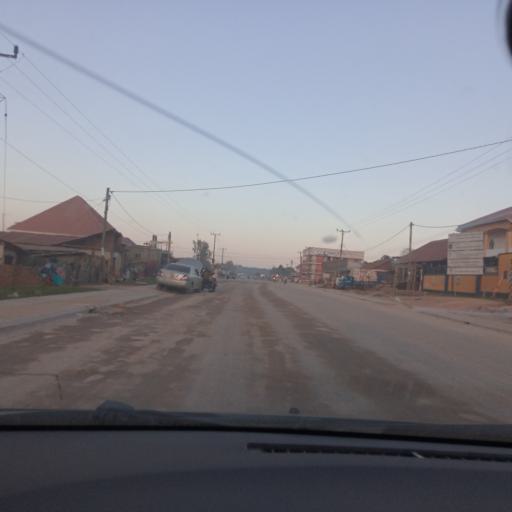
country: UG
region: Central Region
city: Masaka
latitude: -0.3237
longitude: 31.7597
